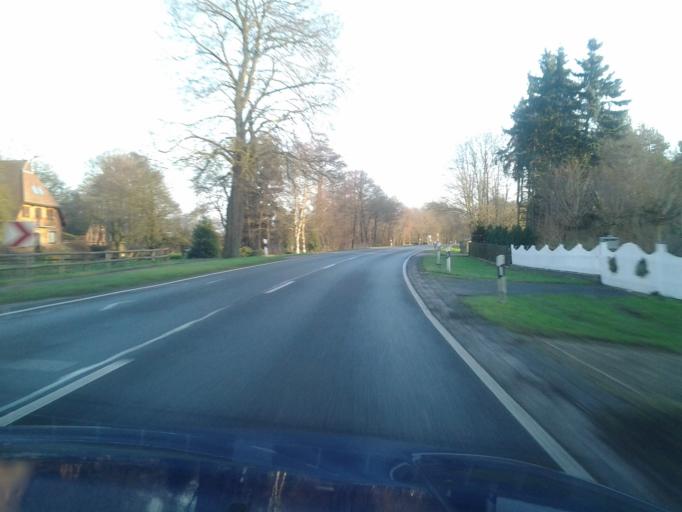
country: DE
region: Lower Saxony
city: Osterholz-Scharmbeck
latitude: 53.1839
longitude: 8.8455
